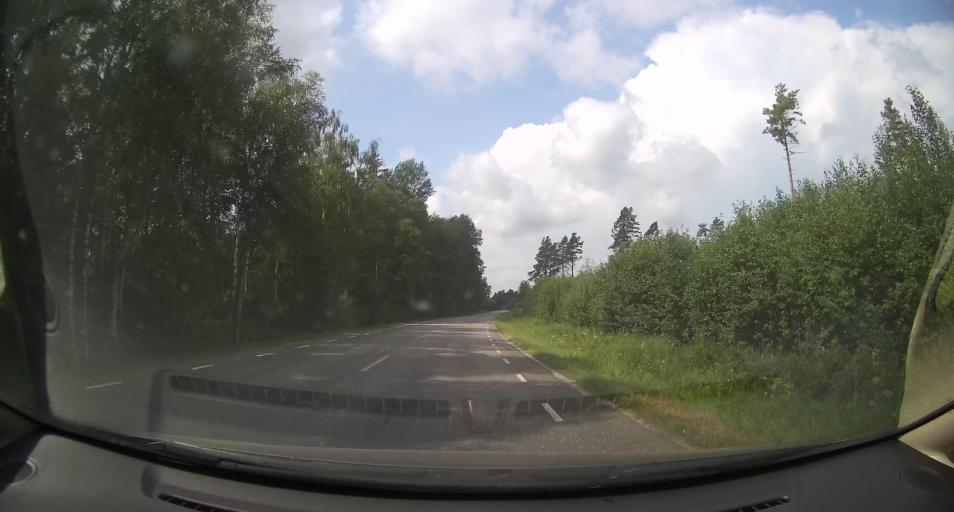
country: EE
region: Laeaene
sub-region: Lihula vald
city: Lihula
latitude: 58.5513
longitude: 23.8623
